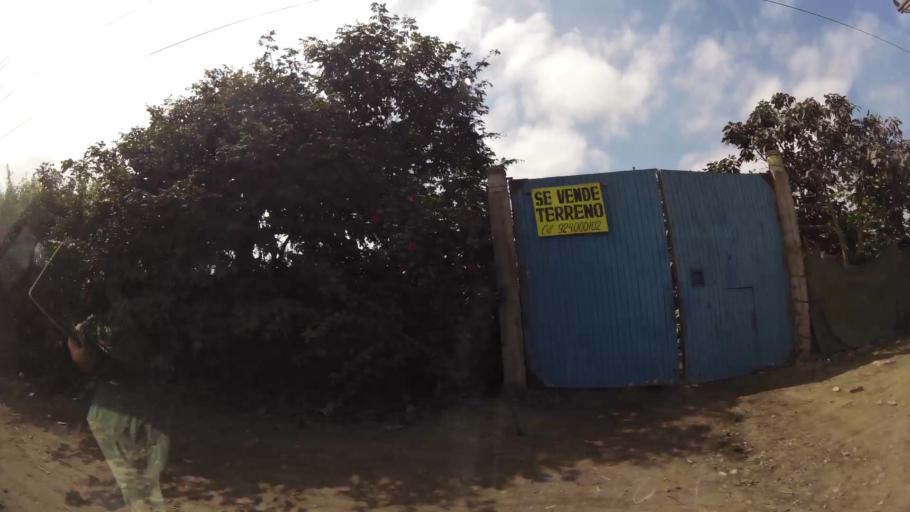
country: PE
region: Lima
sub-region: Provincia de Canete
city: Mala
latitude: -12.7037
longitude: -76.6222
